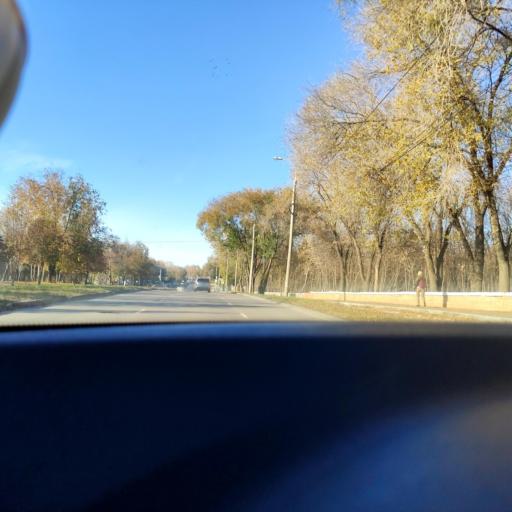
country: RU
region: Samara
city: Samara
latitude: 53.2217
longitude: 50.2375
